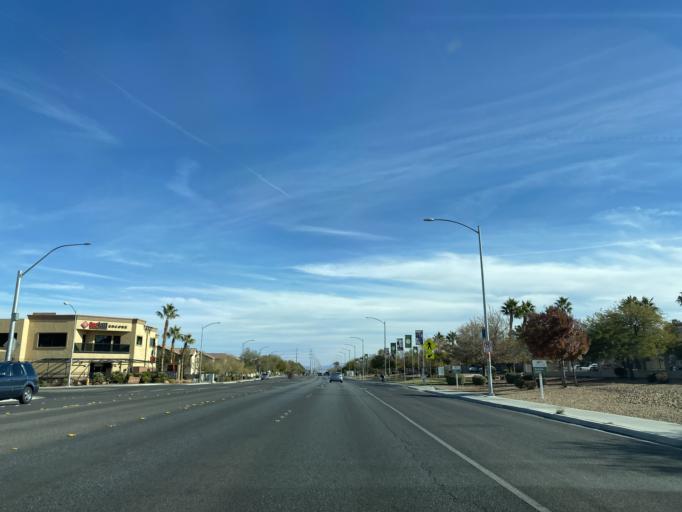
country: US
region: Nevada
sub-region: Clark County
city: Enterprise
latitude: 36.0554
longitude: -115.2889
